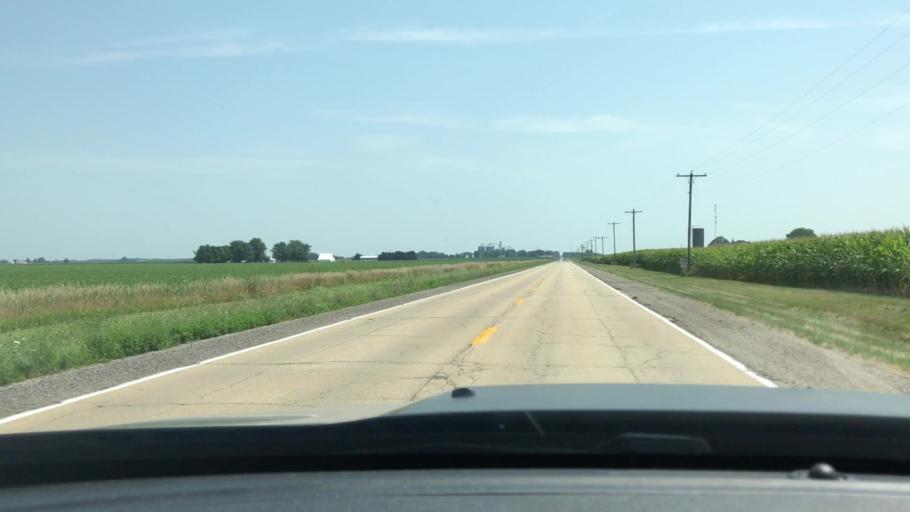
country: US
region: Illinois
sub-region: LaSalle County
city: Sheridan
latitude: 41.4852
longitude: -88.7600
